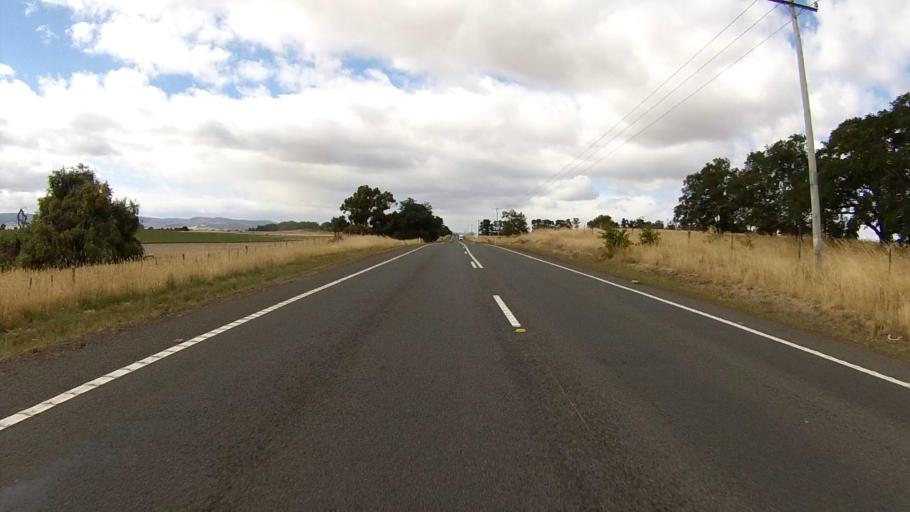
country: AU
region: Tasmania
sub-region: Northern Midlands
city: Evandale
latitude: -41.9055
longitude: 147.4787
